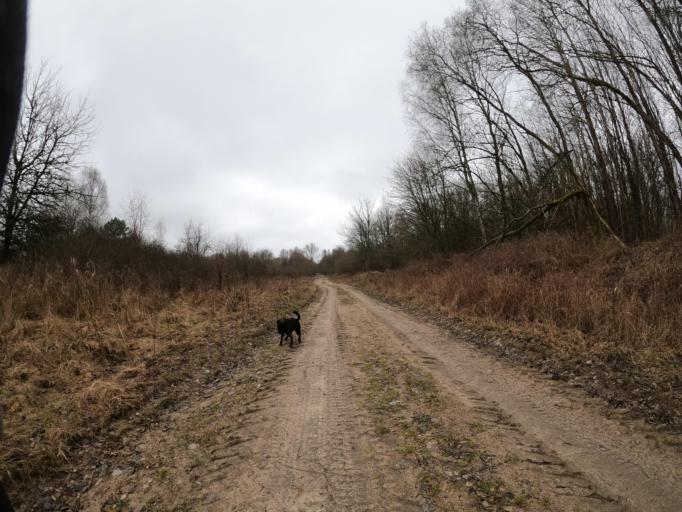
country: PL
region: Greater Poland Voivodeship
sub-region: Powiat zlotowski
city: Sypniewo
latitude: 53.4913
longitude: 16.5647
